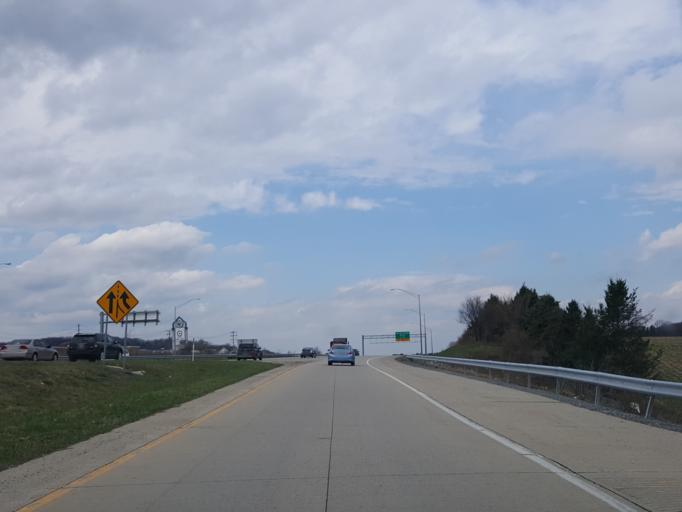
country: US
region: Pennsylvania
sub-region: Berks County
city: Spring Ridge
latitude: 40.3597
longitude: -75.9793
